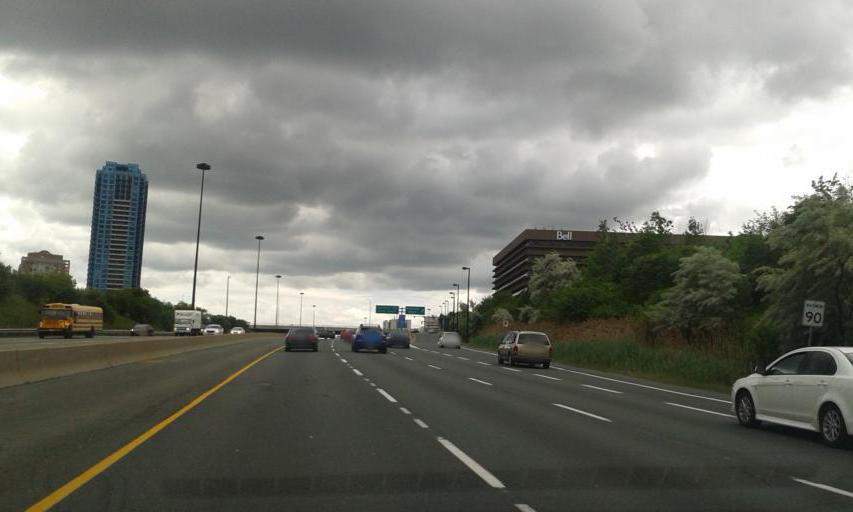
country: CA
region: Ontario
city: Willowdale
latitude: 43.7301
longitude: -79.3307
